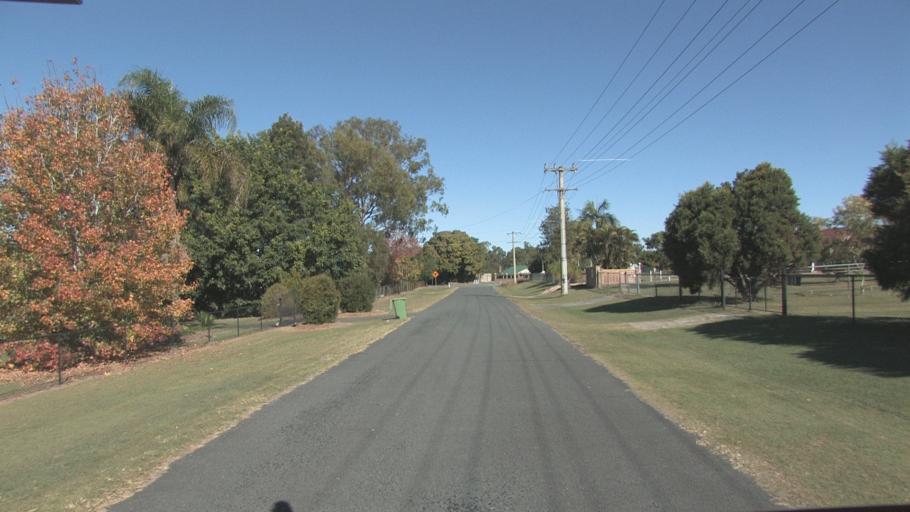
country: AU
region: Queensland
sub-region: Logan
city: Park Ridge South
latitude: -27.7257
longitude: 153.0393
